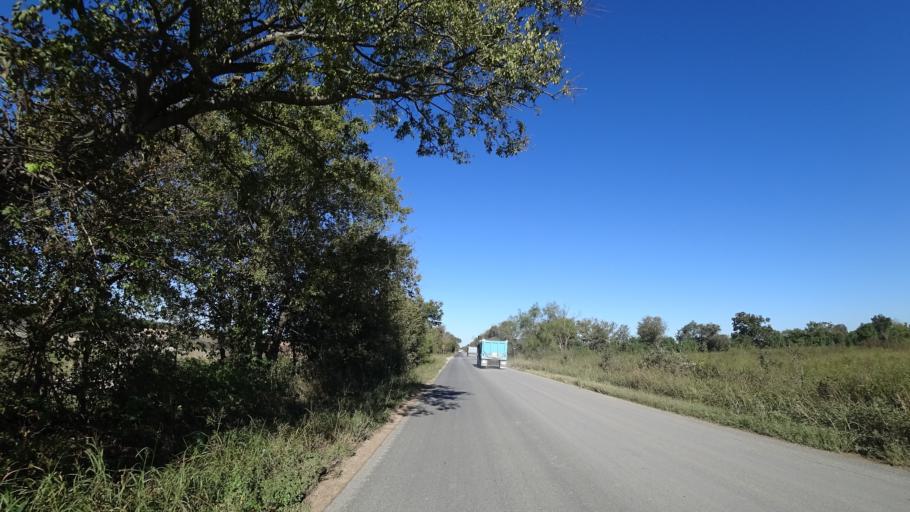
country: US
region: Texas
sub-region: Travis County
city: Austin
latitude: 30.2406
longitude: -97.6659
